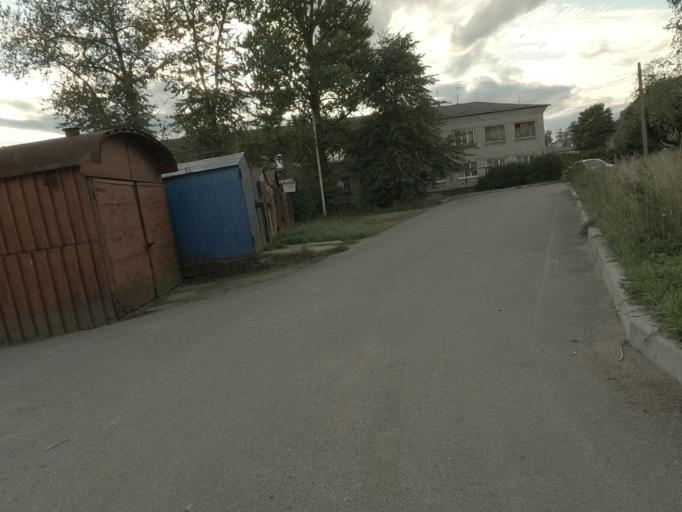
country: RU
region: Leningrad
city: Mga
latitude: 59.7519
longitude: 31.0389
